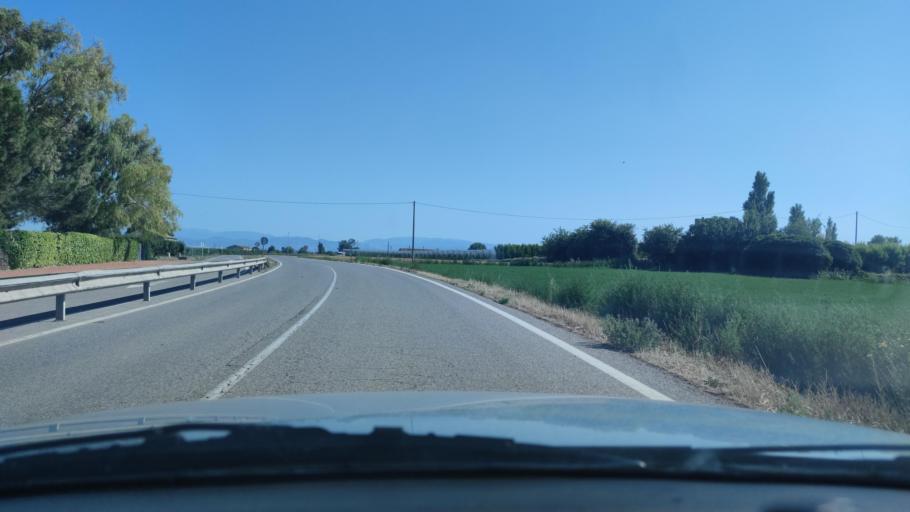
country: ES
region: Catalonia
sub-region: Provincia de Lleida
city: Bellvis
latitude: 41.6611
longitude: 0.8095
